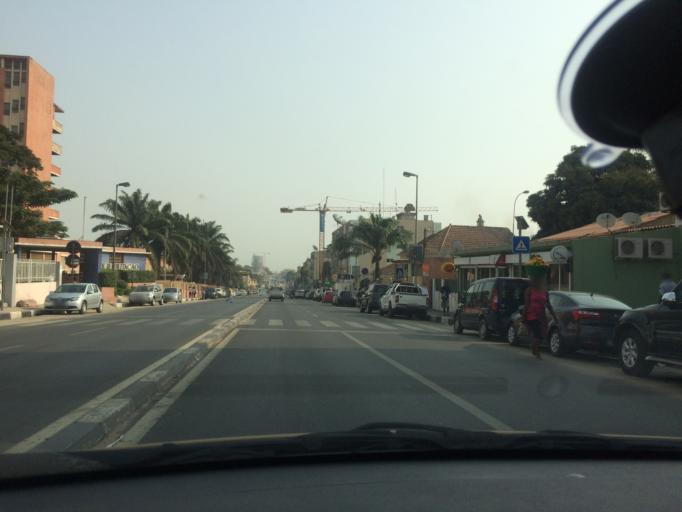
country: AO
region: Luanda
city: Luanda
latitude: -8.8262
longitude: 13.2239
